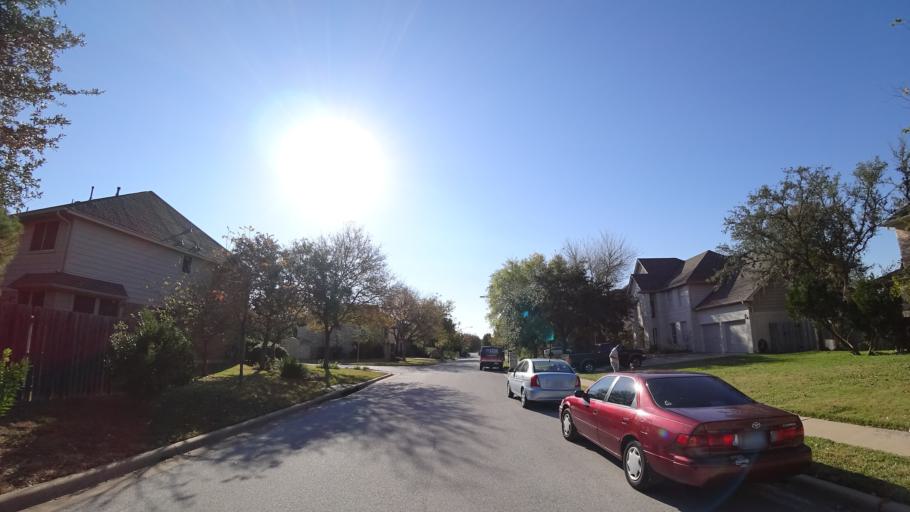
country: US
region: Texas
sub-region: Travis County
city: Shady Hollow
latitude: 30.2238
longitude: -97.8518
